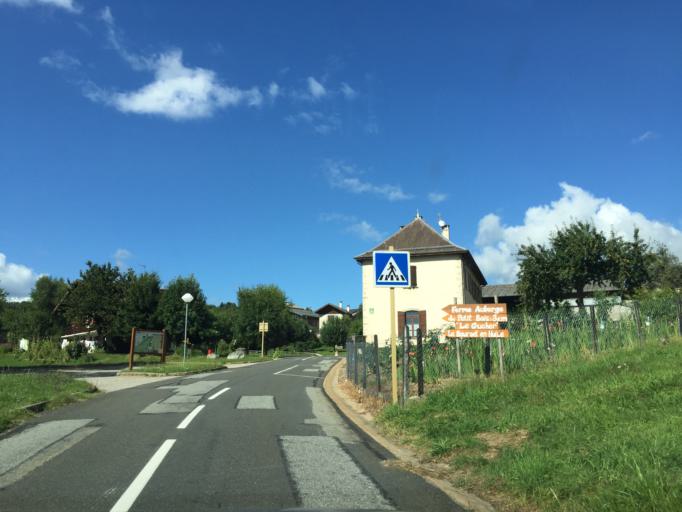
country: FR
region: Rhone-Alpes
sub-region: Departement de la Savoie
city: La Rochette
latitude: 45.4723
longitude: 6.1837
